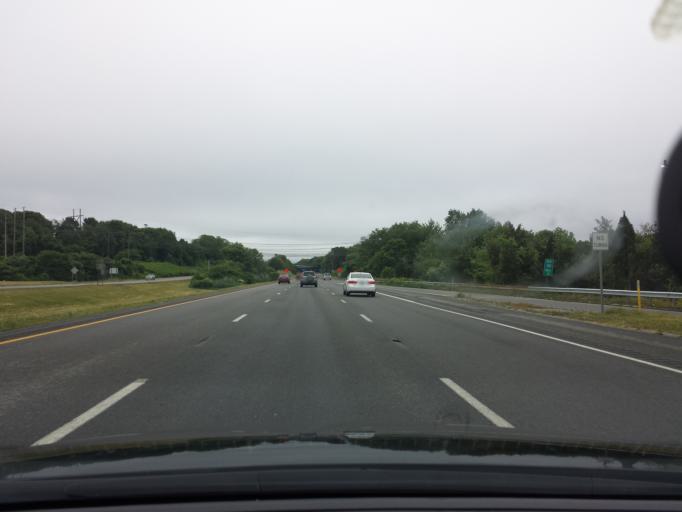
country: US
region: Massachusetts
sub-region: Bristol County
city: Ocean Grove
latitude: 41.7241
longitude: -71.1853
